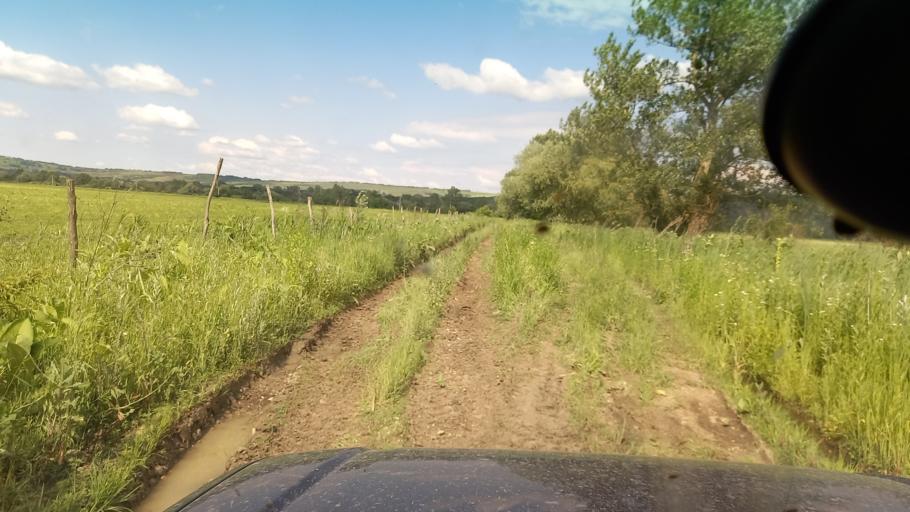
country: RU
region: Krasnodarskiy
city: Shedok
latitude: 44.2119
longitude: 40.9731
